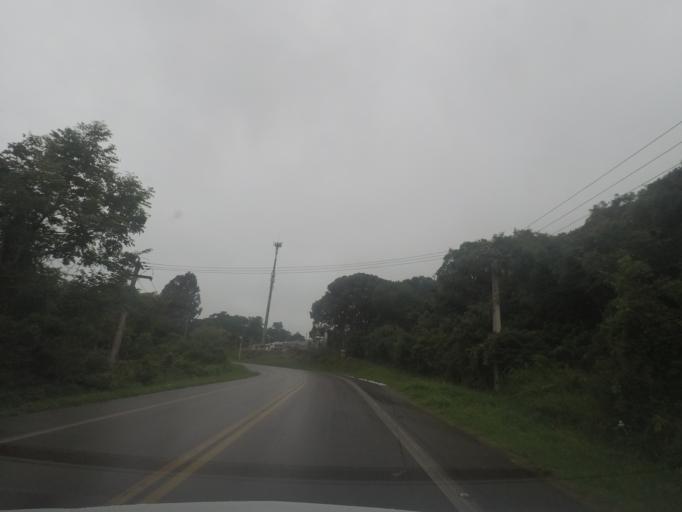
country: BR
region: Parana
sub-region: Colombo
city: Colombo
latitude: -25.3149
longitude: -49.1543
